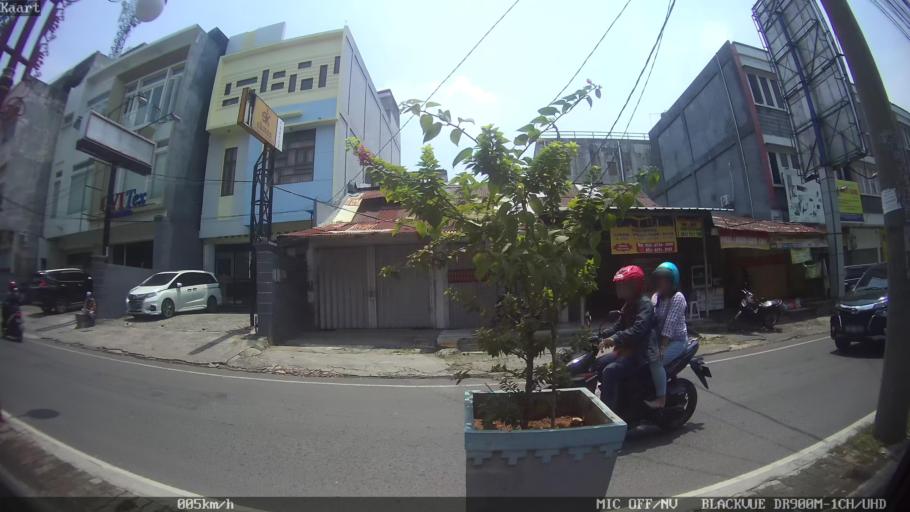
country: ID
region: Lampung
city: Bandarlampung
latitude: -5.4125
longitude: 105.2562
